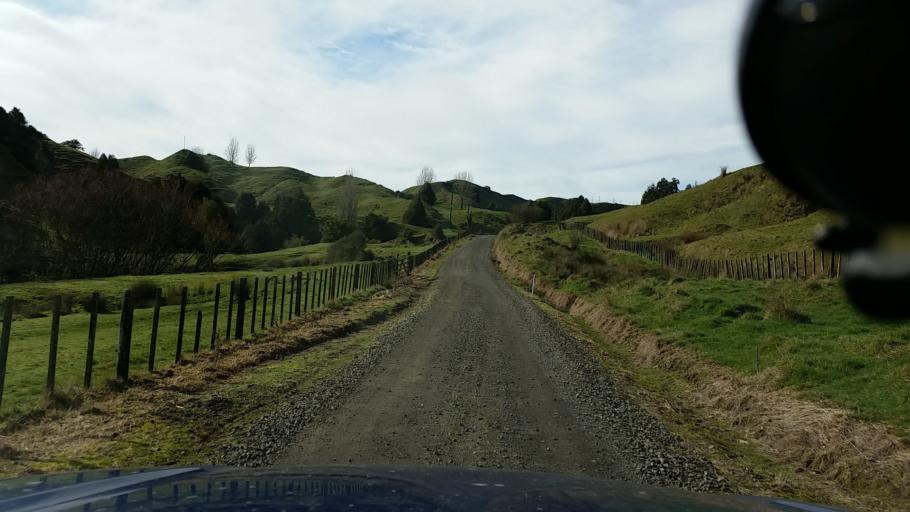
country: NZ
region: Taranaki
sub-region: New Plymouth District
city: Waitara
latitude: -39.0339
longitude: 174.7706
